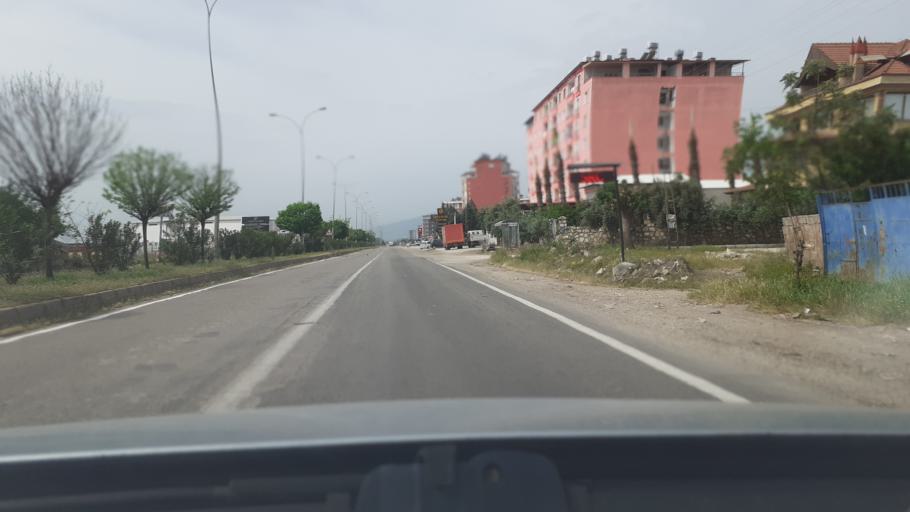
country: TR
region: Hatay
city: Kirikhan
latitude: 36.4825
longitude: 36.3596
